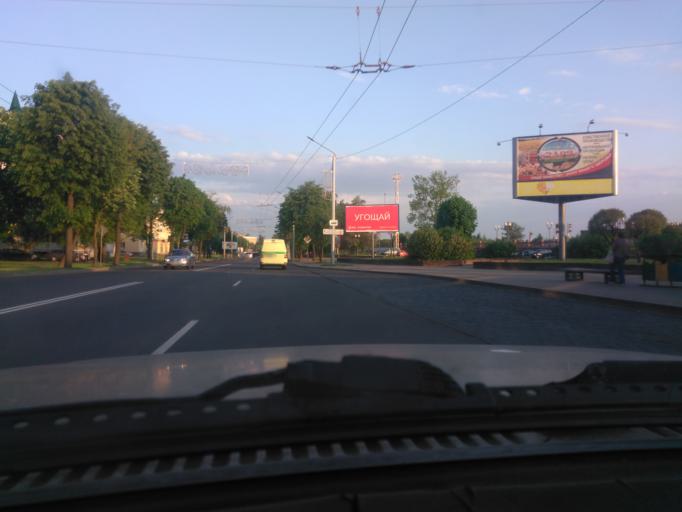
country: BY
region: Mogilev
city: Mahilyow
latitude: 53.9256
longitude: 30.3403
